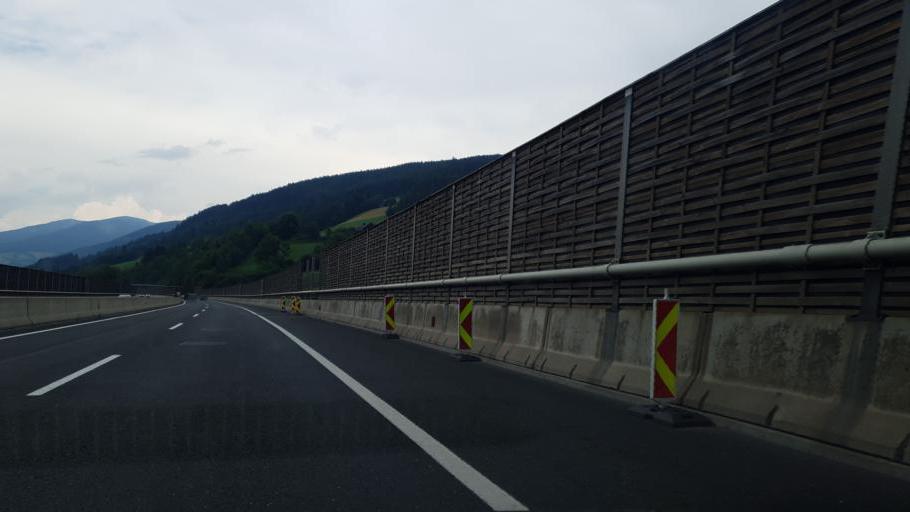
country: AT
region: Carinthia
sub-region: Politischer Bezirk Spittal an der Drau
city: Gmuend
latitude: 46.9361
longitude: 13.6059
